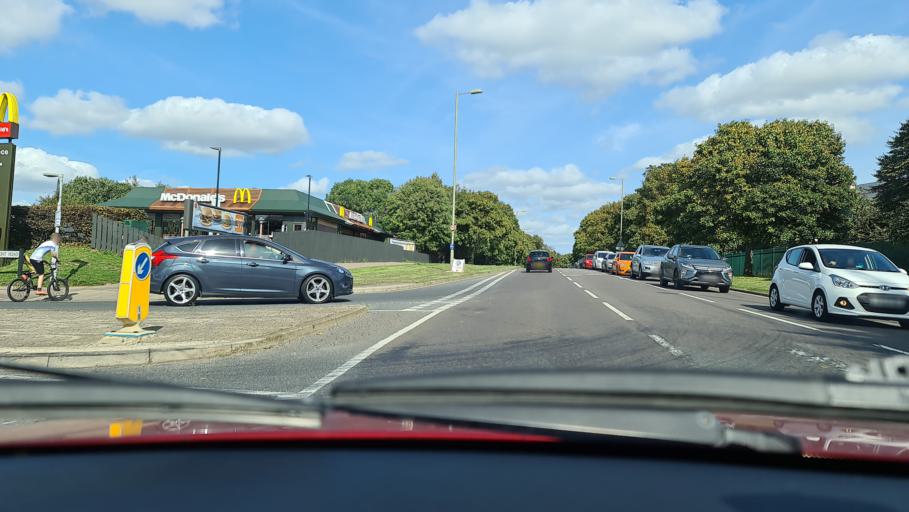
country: GB
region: England
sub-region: Oxfordshire
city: Banbury
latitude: 52.0714
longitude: -1.3443
